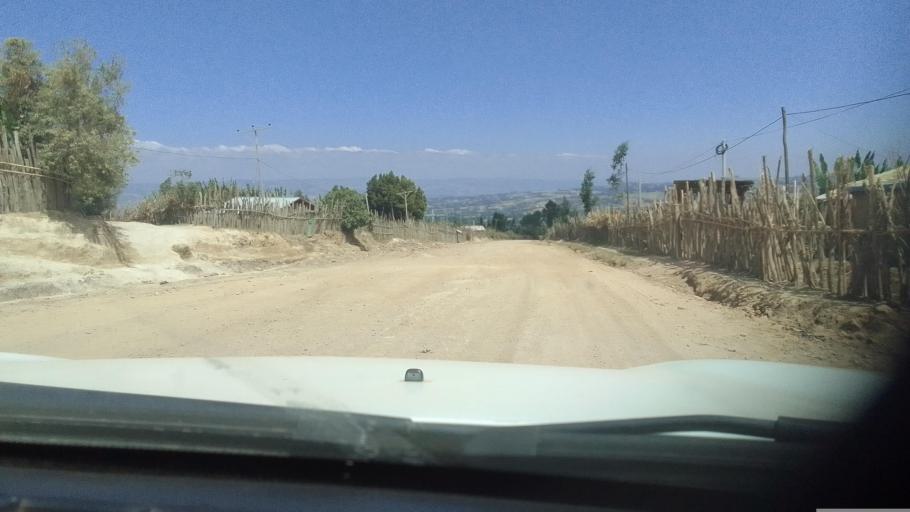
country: ET
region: Oromiya
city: Hagere Hiywet
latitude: 8.8471
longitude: 37.8873
